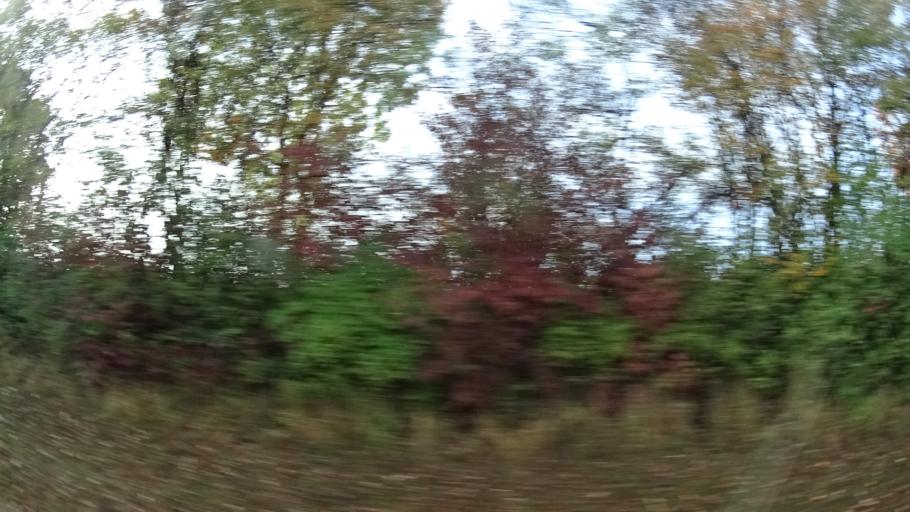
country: DE
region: Hesse
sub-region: Regierungsbezirk Darmstadt
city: Hirzenhain
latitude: 50.4147
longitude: 9.1213
